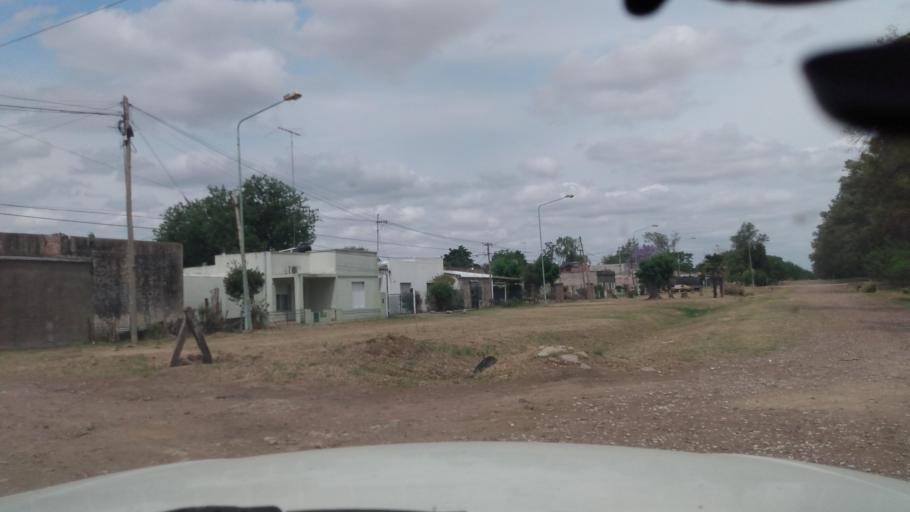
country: AR
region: Buenos Aires
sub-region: Partido de Lujan
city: Lujan
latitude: -34.5591
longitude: -59.2076
